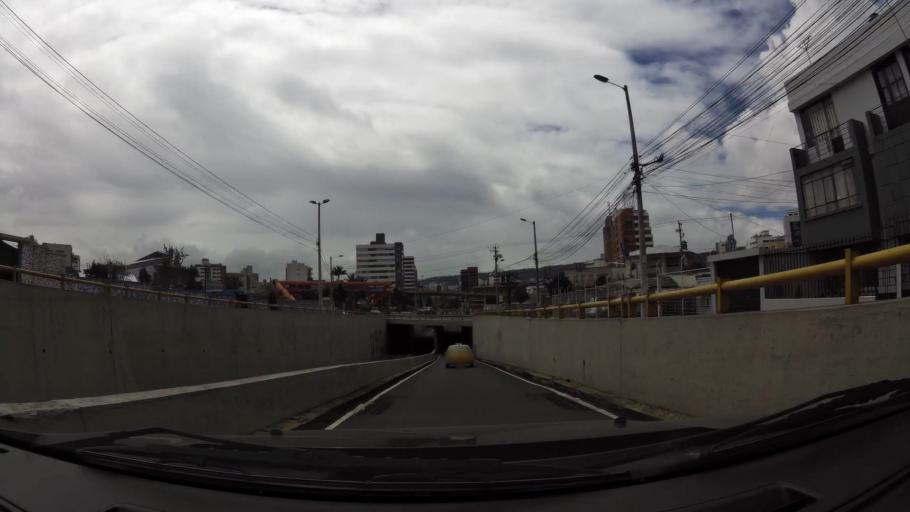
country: EC
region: Pichincha
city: Quito
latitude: -0.1840
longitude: -78.4912
